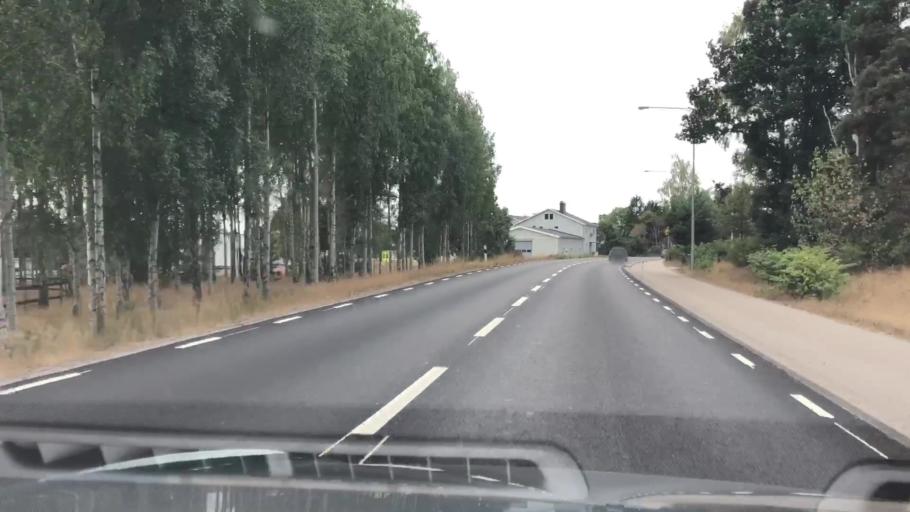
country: SE
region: Blekinge
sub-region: Karlskrona Kommun
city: Jaemjoe
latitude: 56.1950
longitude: 15.8469
